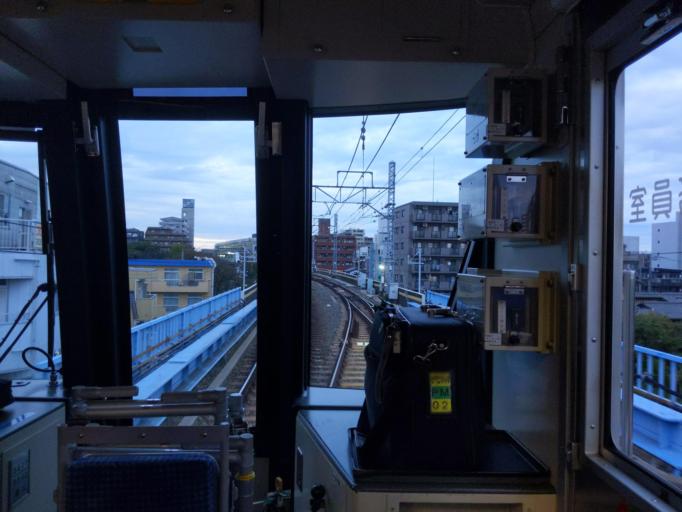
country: JP
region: Saitama
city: Yashio-shi
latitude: 35.7743
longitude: 139.8318
